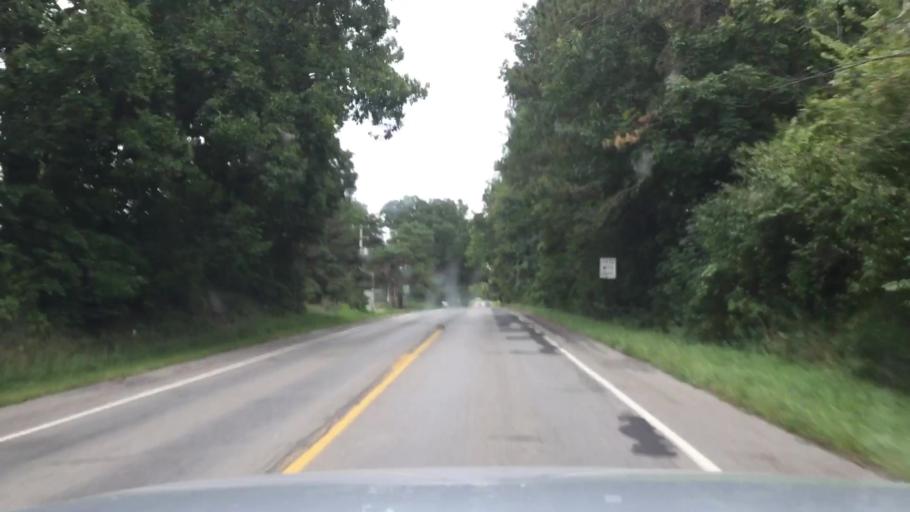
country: US
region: Michigan
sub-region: Genesee County
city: Argentine
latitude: 42.7967
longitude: -83.8576
